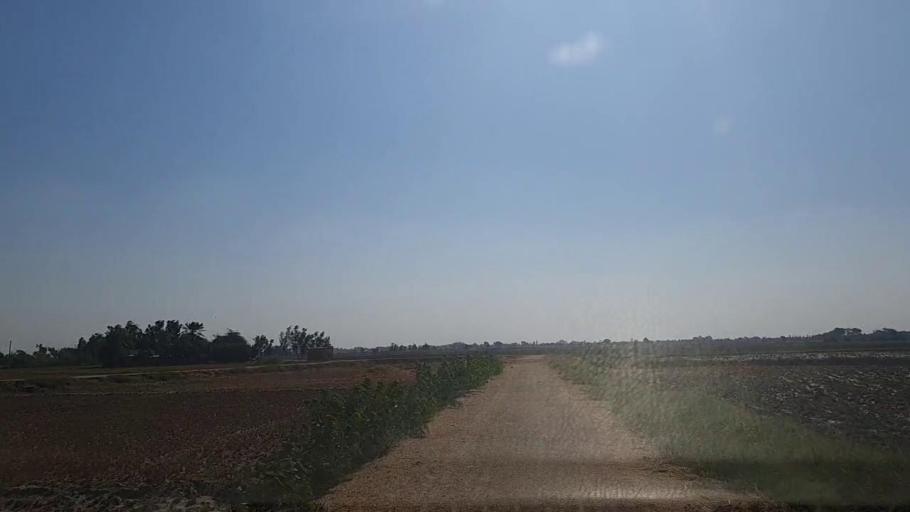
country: PK
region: Sindh
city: Thatta
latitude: 24.7707
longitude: 67.9509
